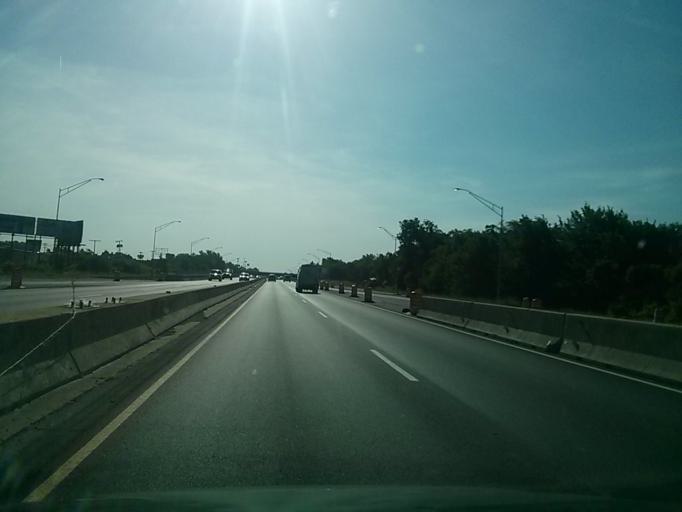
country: US
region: Oklahoma
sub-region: Tulsa County
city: Tulsa
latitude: 36.1596
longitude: -95.9370
